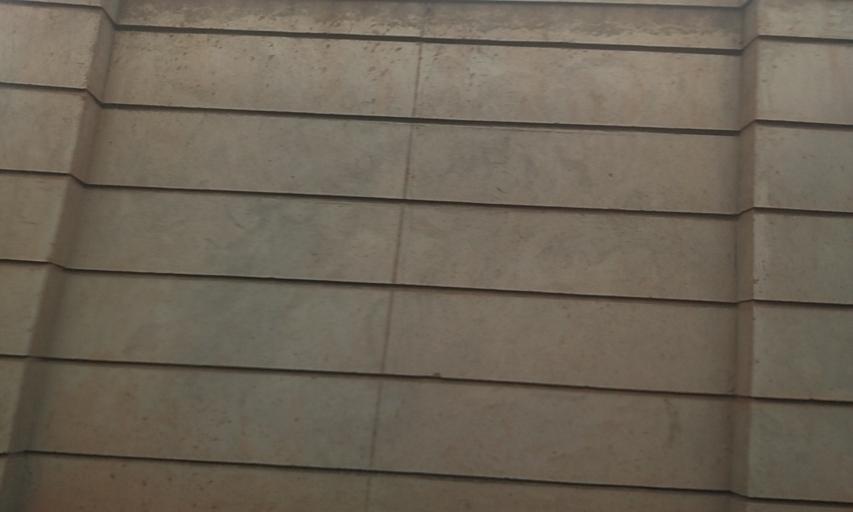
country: UG
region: Central Region
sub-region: Wakiso District
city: Kajansi
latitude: 0.2724
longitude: 32.5246
